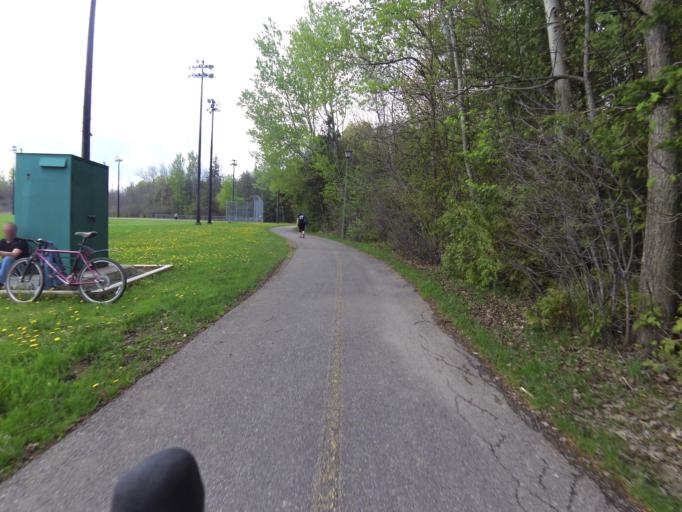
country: CA
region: Ontario
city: Bells Corners
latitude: 45.2760
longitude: -75.7938
